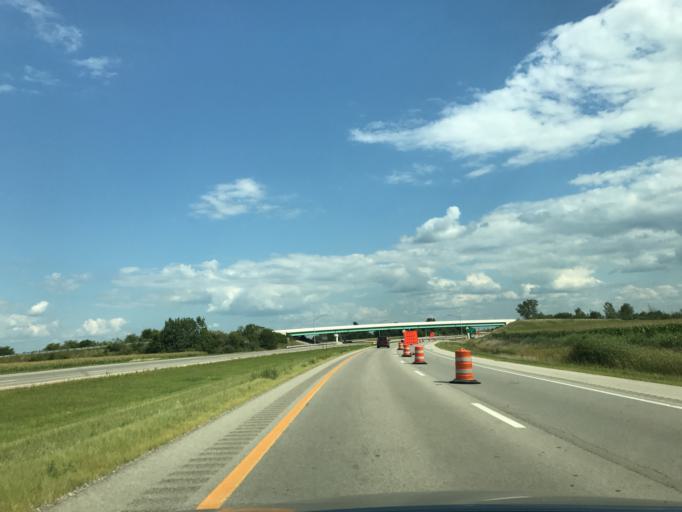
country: US
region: Ohio
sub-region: Van Wert County
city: Van Wert
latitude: 40.8848
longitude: -84.5320
